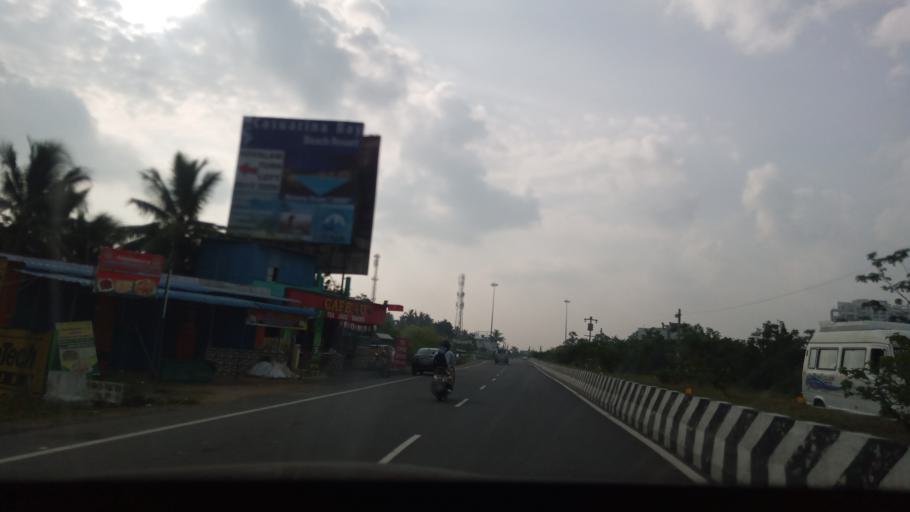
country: IN
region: Tamil Nadu
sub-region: Kancheepuram
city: Injambakkam
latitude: 12.7810
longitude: 80.2470
